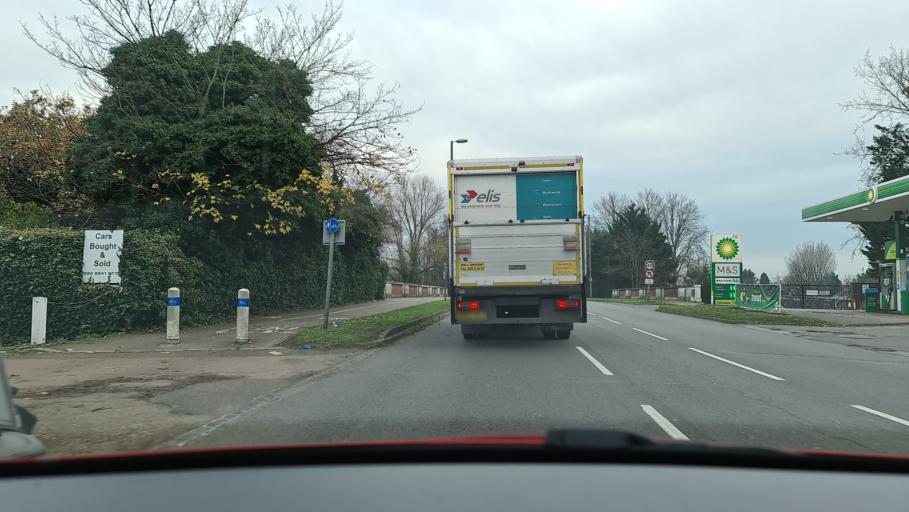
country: GB
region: England
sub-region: Surrey
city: East Molesey
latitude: 51.4016
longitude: -0.3431
